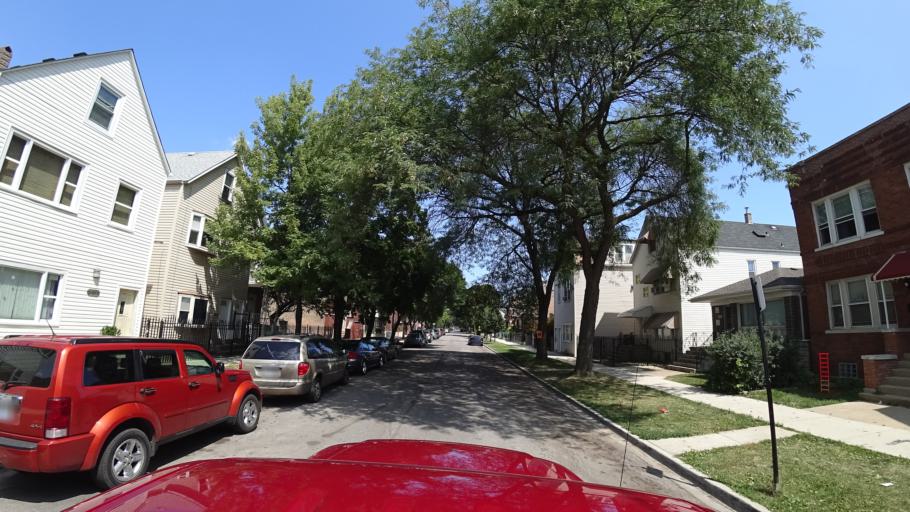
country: US
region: Illinois
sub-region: Cook County
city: Chicago
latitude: 41.8126
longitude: -87.6931
